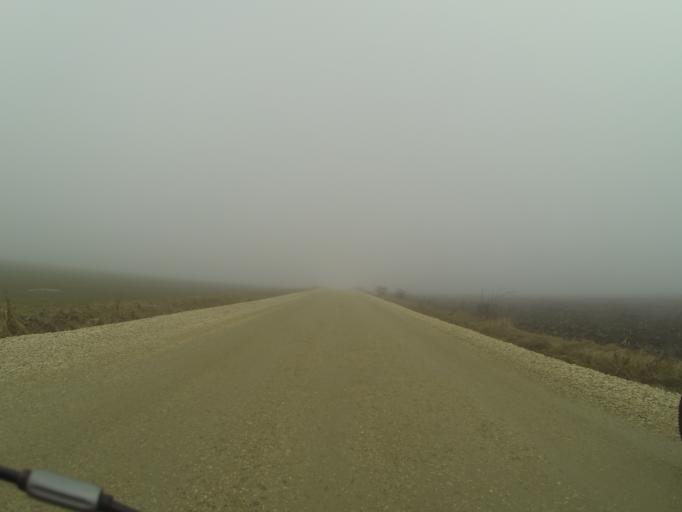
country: RO
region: Mehedinti
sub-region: Comuna Balacita
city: Gvardinita
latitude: 44.4313
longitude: 23.1327
